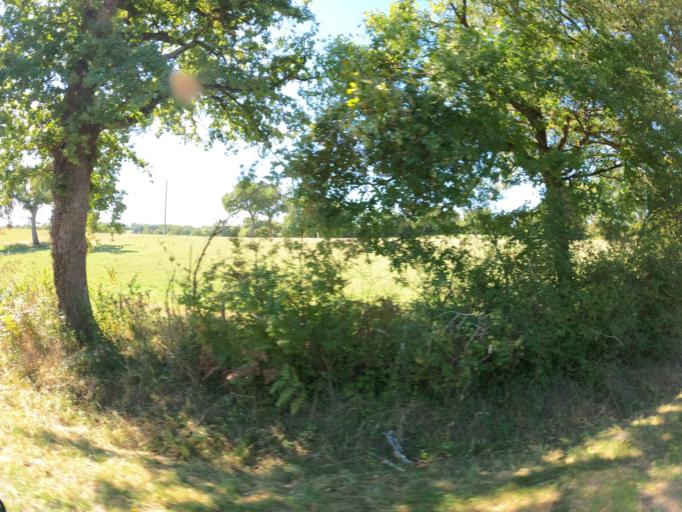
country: FR
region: Limousin
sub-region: Departement de la Haute-Vienne
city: Le Dorat
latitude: 46.2344
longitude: 1.0588
